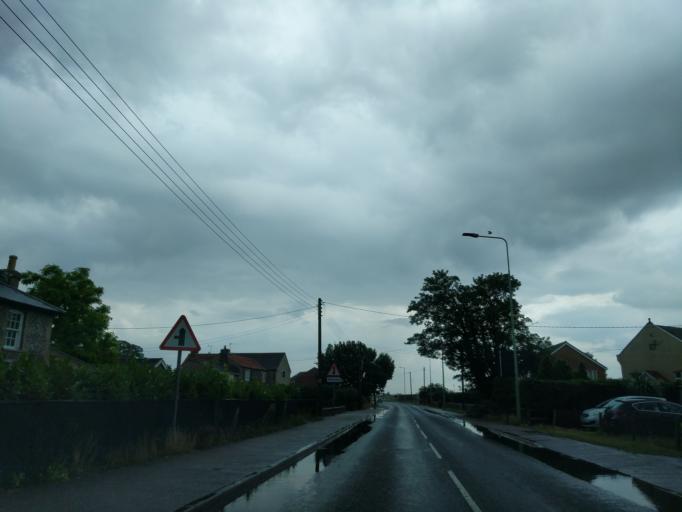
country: GB
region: England
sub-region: Suffolk
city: Lakenheath
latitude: 52.3671
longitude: 0.4882
